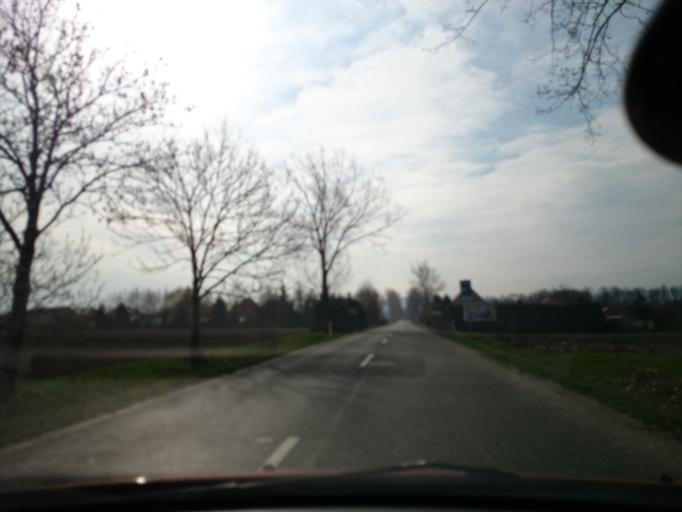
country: PL
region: Opole Voivodeship
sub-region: Powiat nyski
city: Glucholazy
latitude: 50.3479
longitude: 17.3846
